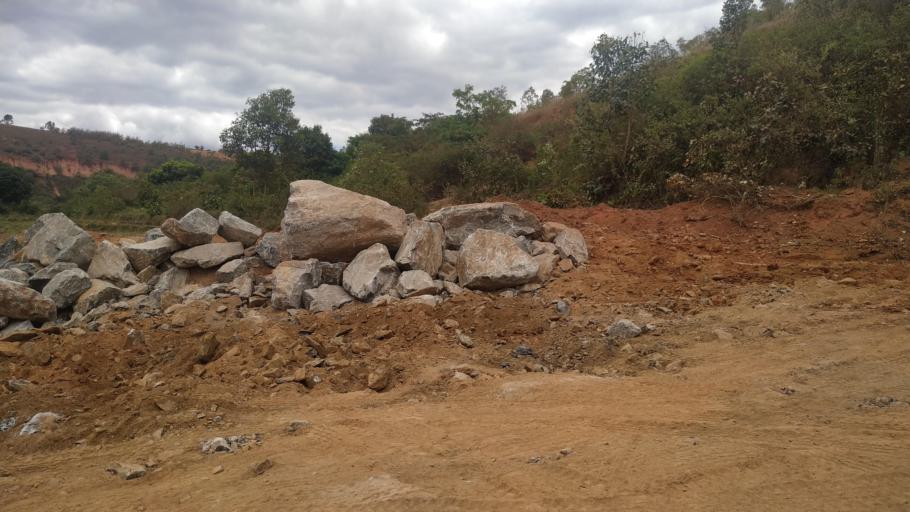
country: MG
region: Alaotra Mangoro
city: Ambatondrazaka
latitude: -18.0199
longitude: 48.2573
